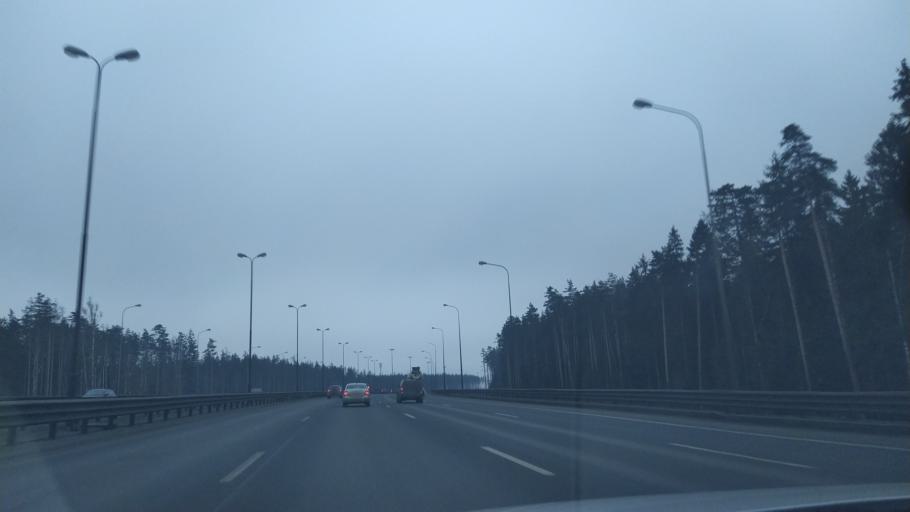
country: RU
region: Leningrad
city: Yanino Vtoroye
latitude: 59.9670
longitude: 30.5525
